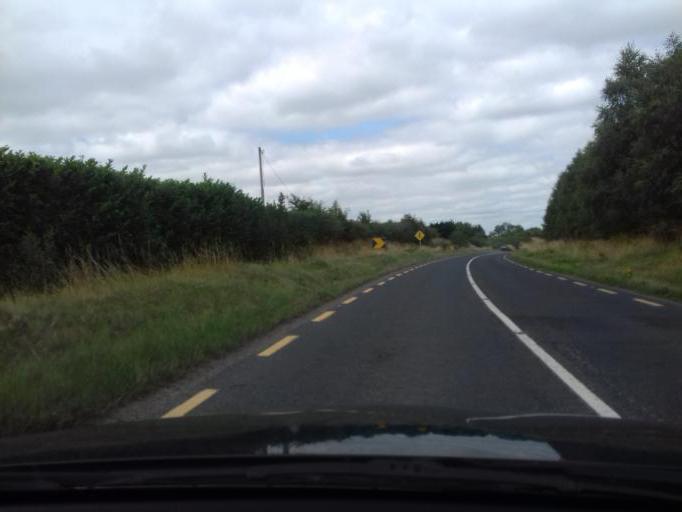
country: IE
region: Leinster
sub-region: County Carlow
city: Tullow
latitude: 52.7870
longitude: -6.7545
